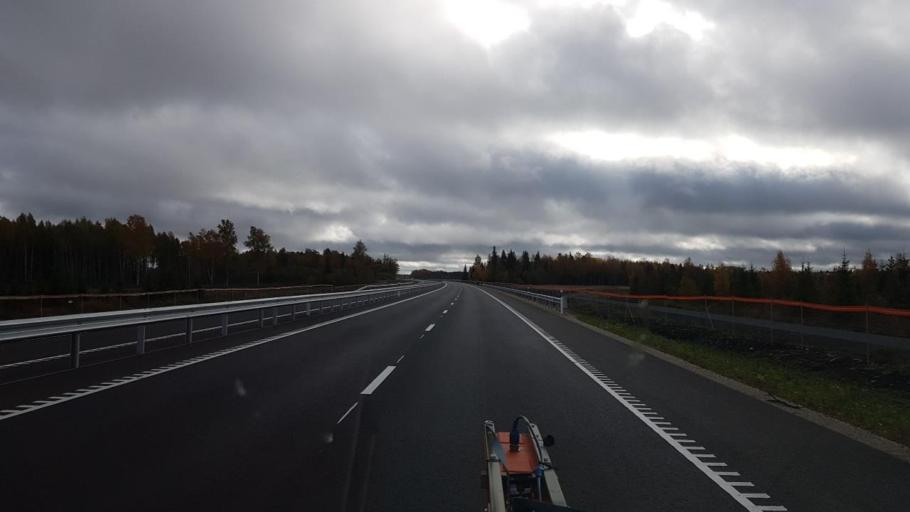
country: EE
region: Jaervamaa
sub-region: Paide linn
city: Paide
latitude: 59.0117
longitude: 25.5577
